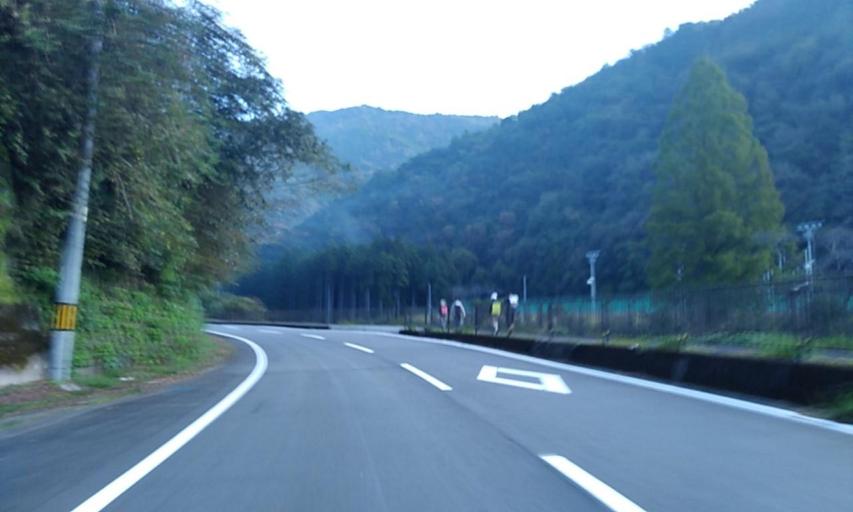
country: JP
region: Wakayama
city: Shingu
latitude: 33.7304
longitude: 135.9102
